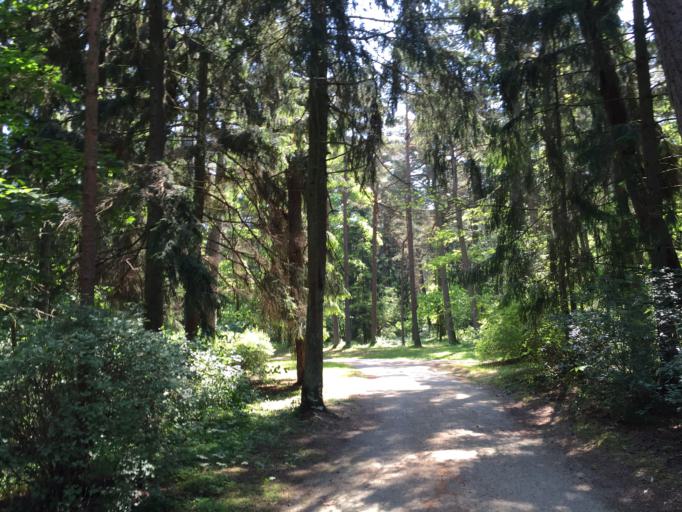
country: LT
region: Klaipedos apskritis
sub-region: Klaipeda
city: Palanga
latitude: 55.9106
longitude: 21.0570
